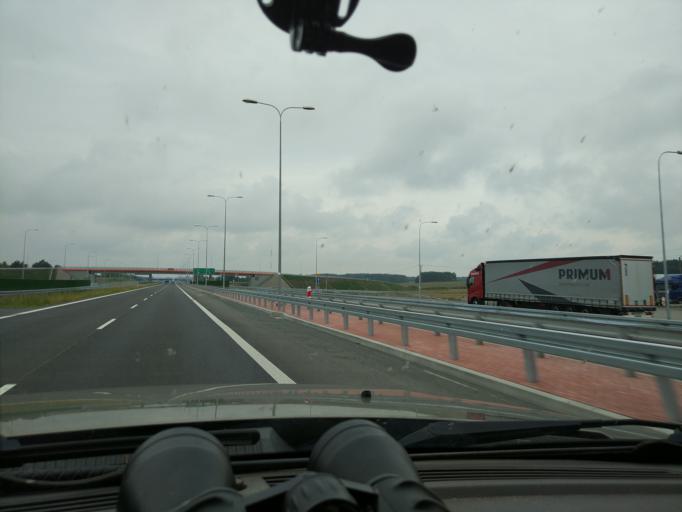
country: PL
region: Podlasie
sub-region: Powiat zambrowski
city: Szumowo
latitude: 52.8661
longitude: 22.0128
